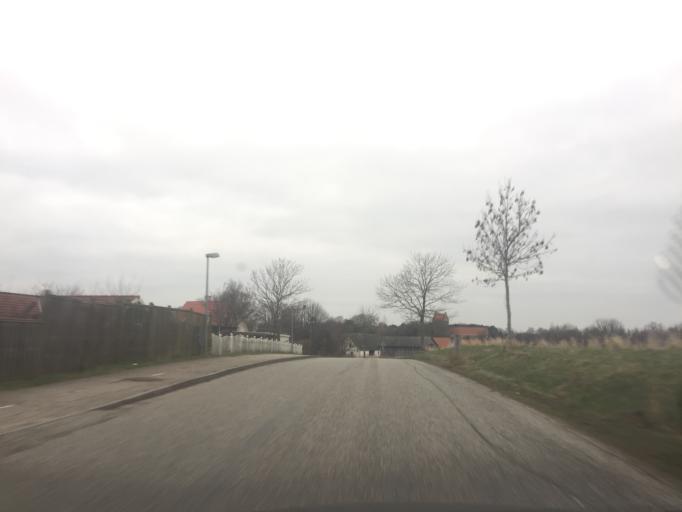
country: DK
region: Capital Region
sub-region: Halsnaes Kommune
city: Liseleje
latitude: 55.9925
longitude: 11.9722
